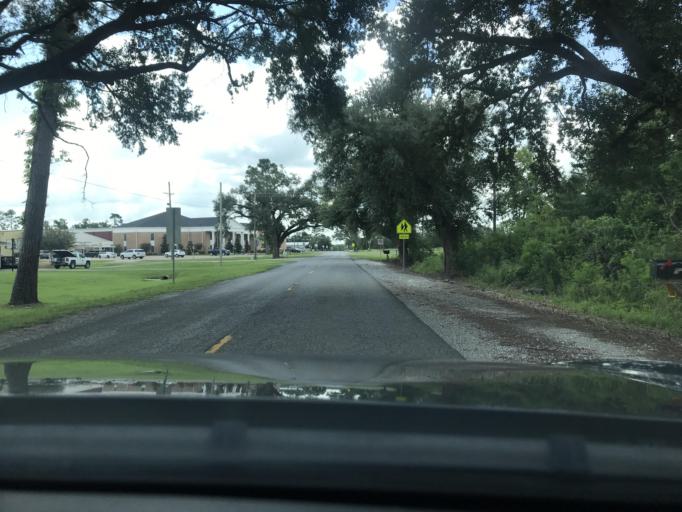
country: US
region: Louisiana
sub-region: Calcasieu Parish
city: Moss Bluff
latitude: 30.3051
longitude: -93.1919
